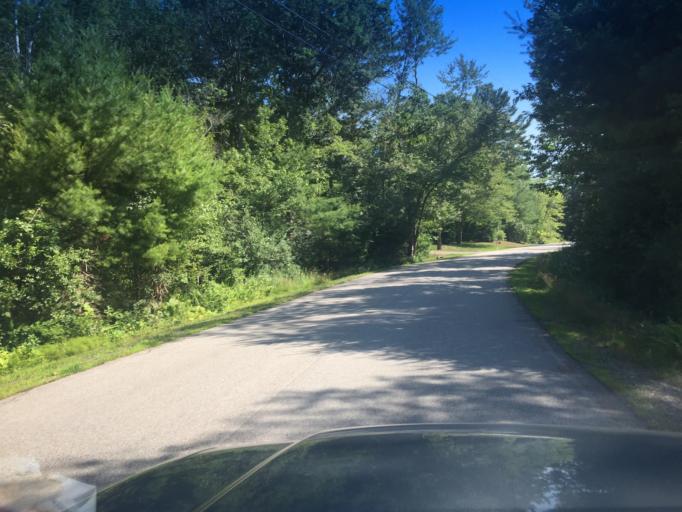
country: US
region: Maine
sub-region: York County
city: York Harbor
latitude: 43.1589
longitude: -70.6439
